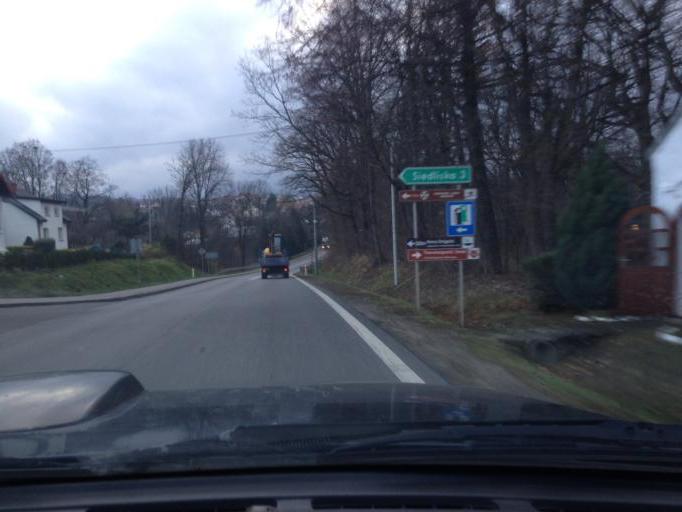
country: PL
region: Subcarpathian Voivodeship
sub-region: Powiat jasielski
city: Nowy Zmigrod
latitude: 49.6089
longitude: 21.5289
